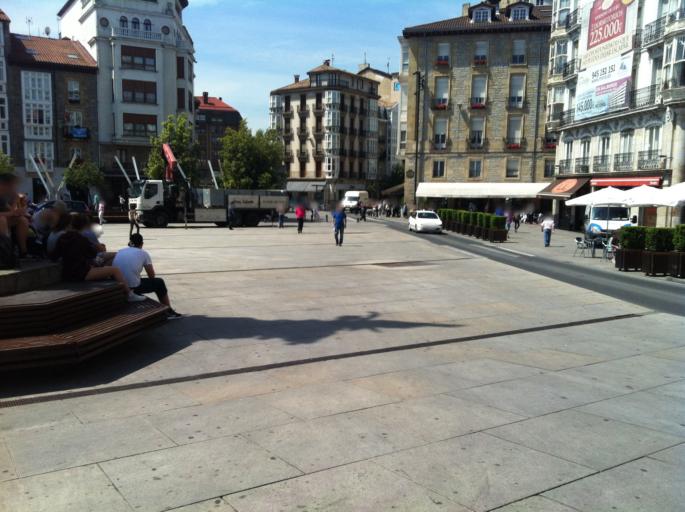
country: ES
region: Basque Country
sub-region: Provincia de Alava
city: Gasteiz / Vitoria
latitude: 42.8467
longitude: -2.6732
